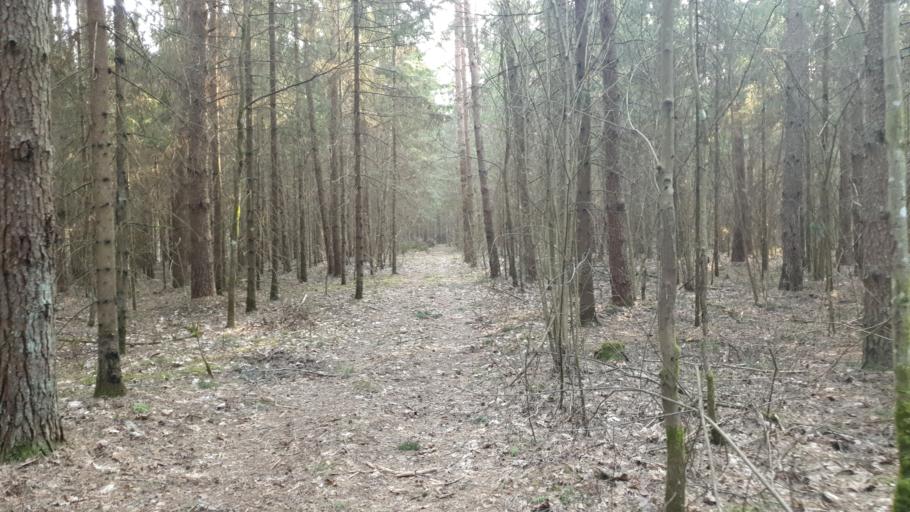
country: LT
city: Nemencine
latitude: 54.8750
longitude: 25.5725
